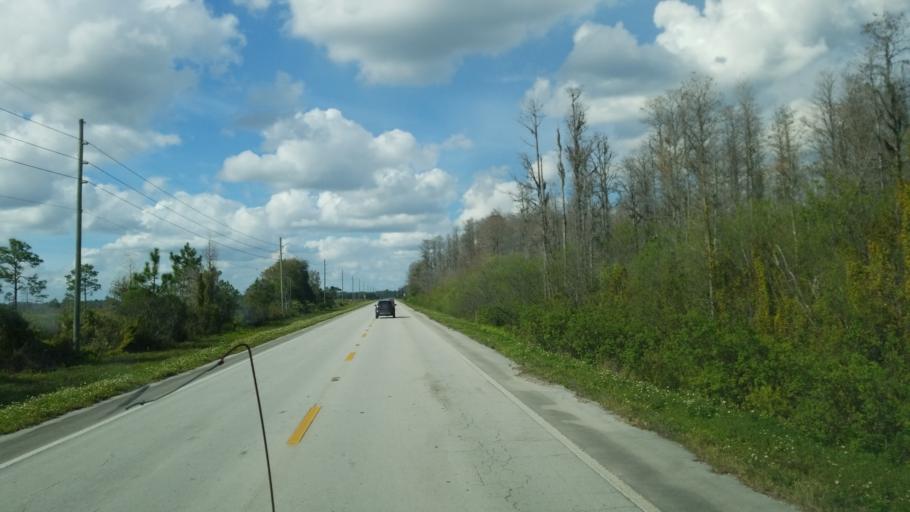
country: US
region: Florida
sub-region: Osceola County
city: Saint Cloud
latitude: 28.0658
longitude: -81.0636
